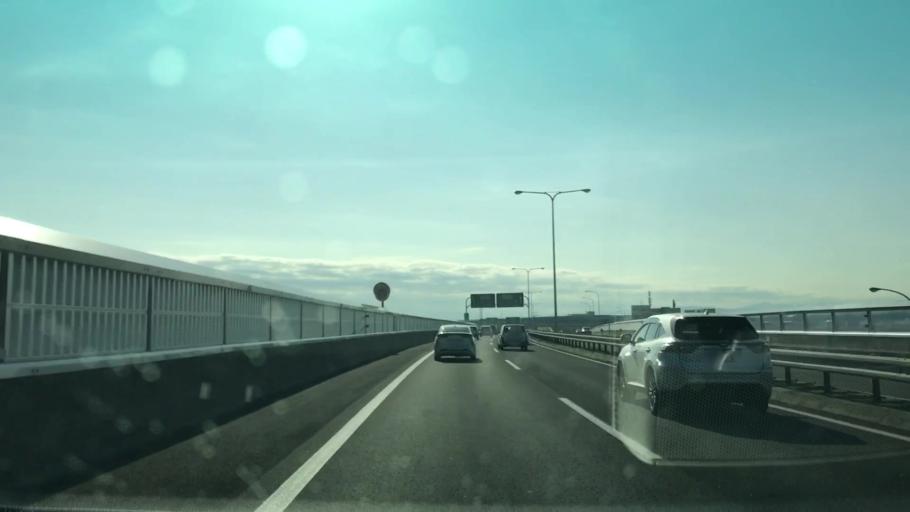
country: JP
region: Hokkaido
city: Sapporo
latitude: 43.0824
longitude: 141.4194
